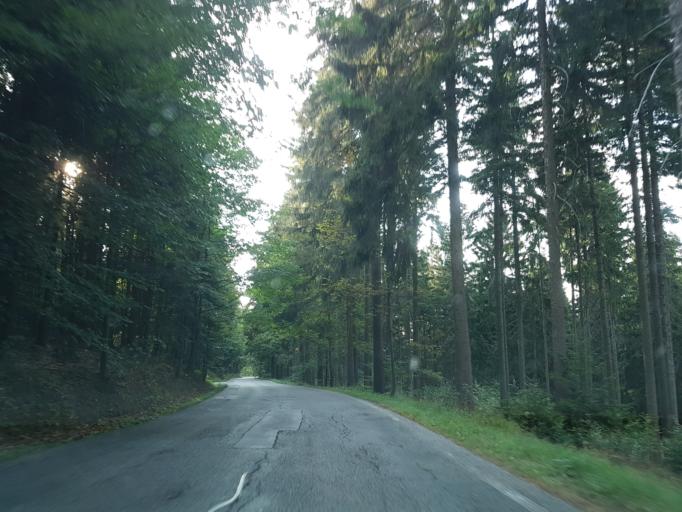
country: CZ
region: Liberecky
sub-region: Okres Jablonec nad Nisou
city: Jablonec nad Nisou
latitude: 50.7100
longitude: 15.1965
